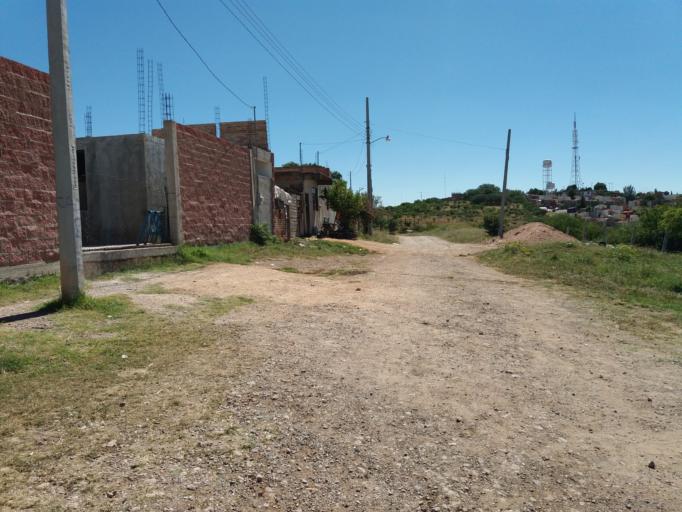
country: MX
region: Aguascalientes
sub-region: Aguascalientes
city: Aguascalientes
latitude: 21.8673
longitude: -102.2291
